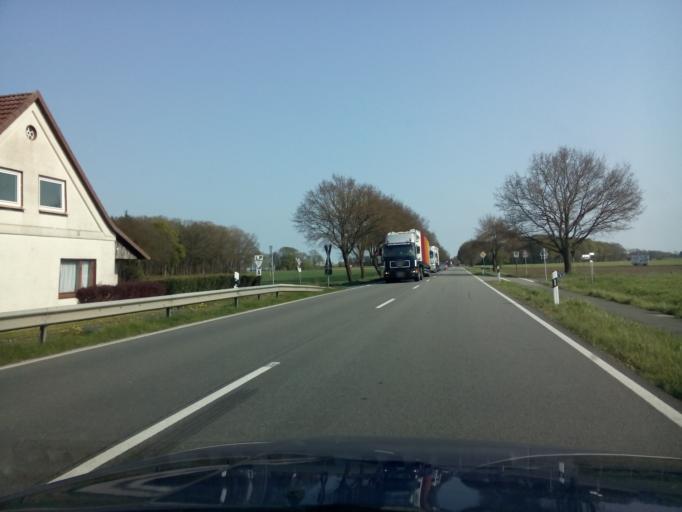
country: DE
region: Lower Saxony
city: Asendorf
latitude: 52.7856
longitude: 8.9931
